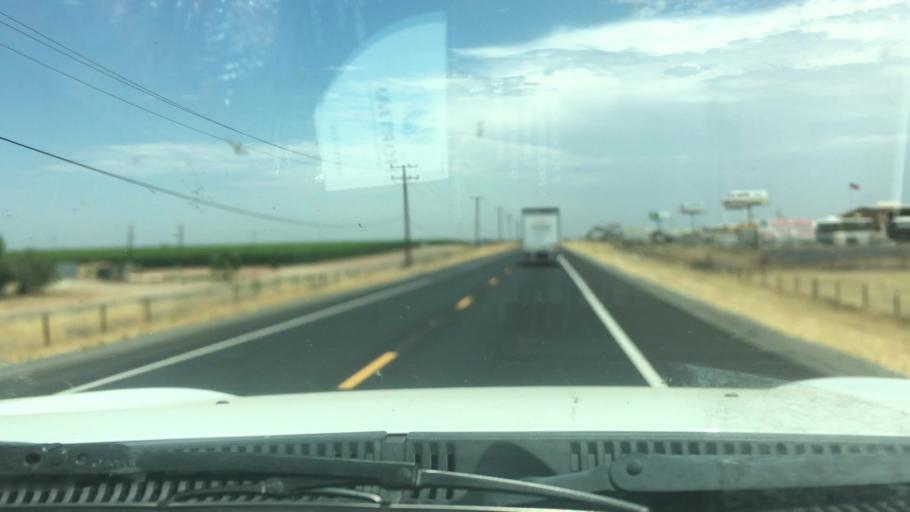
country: US
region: California
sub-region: Tulare County
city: Terra Bella
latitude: 35.9454
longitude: -119.0537
